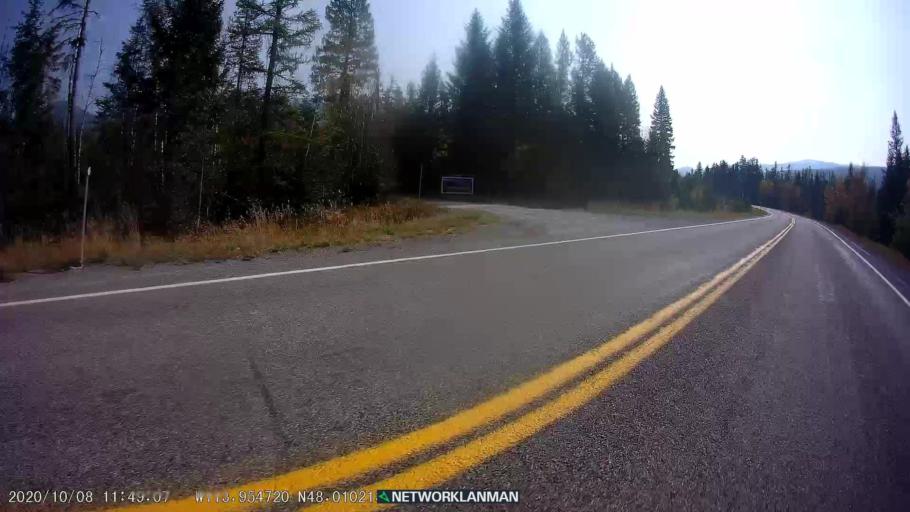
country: US
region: Montana
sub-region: Flathead County
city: Bigfork
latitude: 48.0091
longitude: -113.9558
